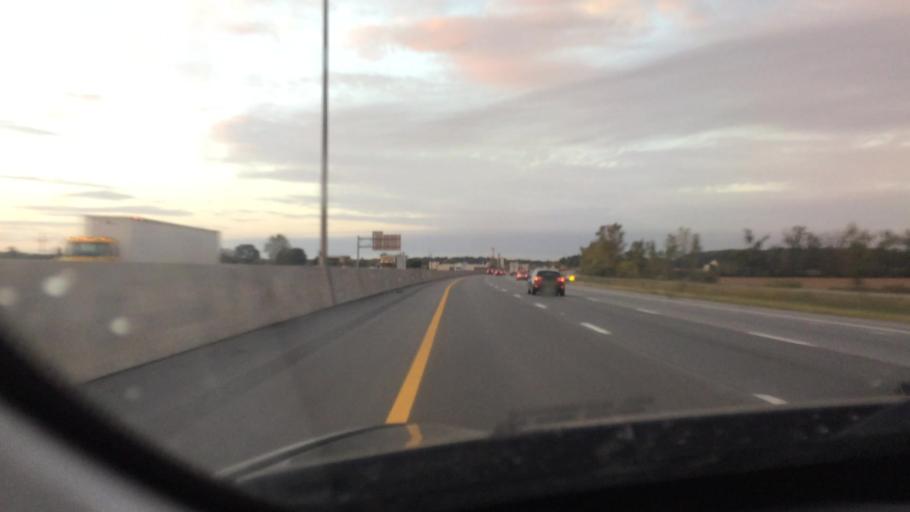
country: US
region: Ohio
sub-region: Wood County
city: North Baltimore
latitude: 41.1669
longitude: -83.6500
